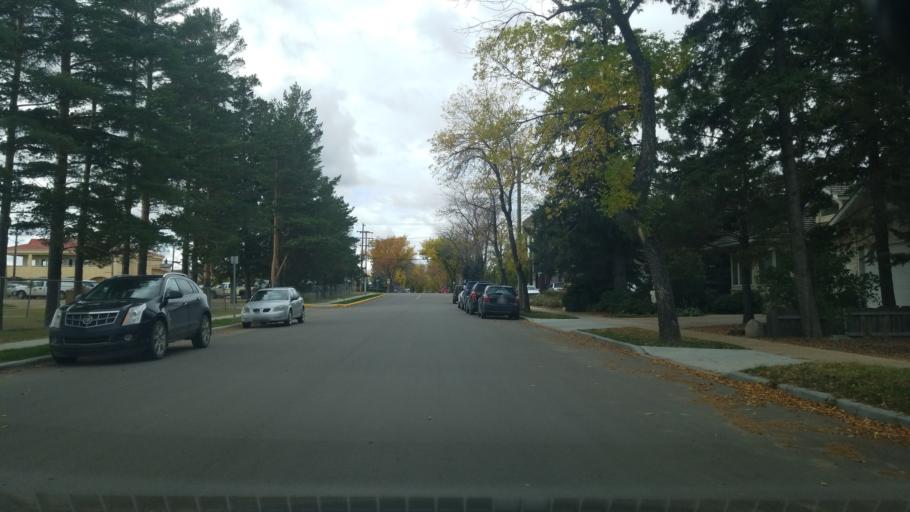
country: CA
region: Saskatchewan
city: Lloydminster
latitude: 53.2798
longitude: -110.0086
